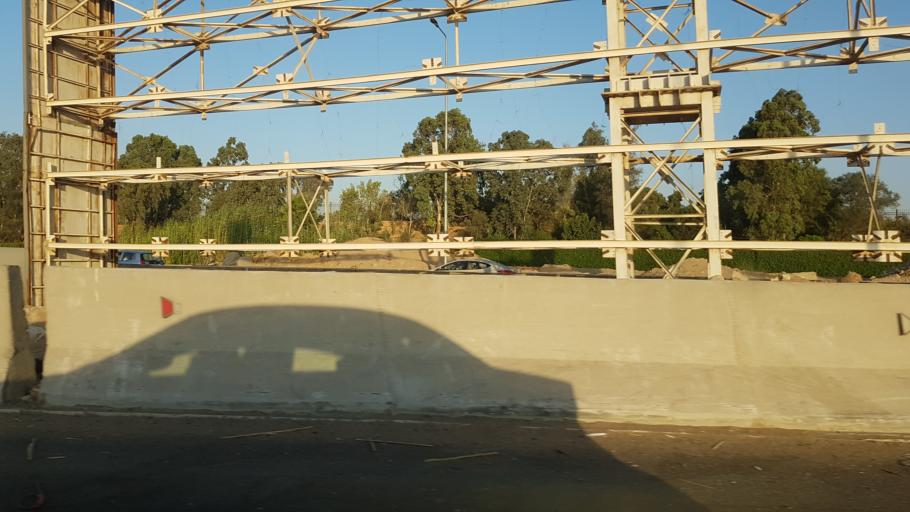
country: EG
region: Muhafazat al Qalyubiyah
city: Al Khankah
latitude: 30.0755
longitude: 31.4337
